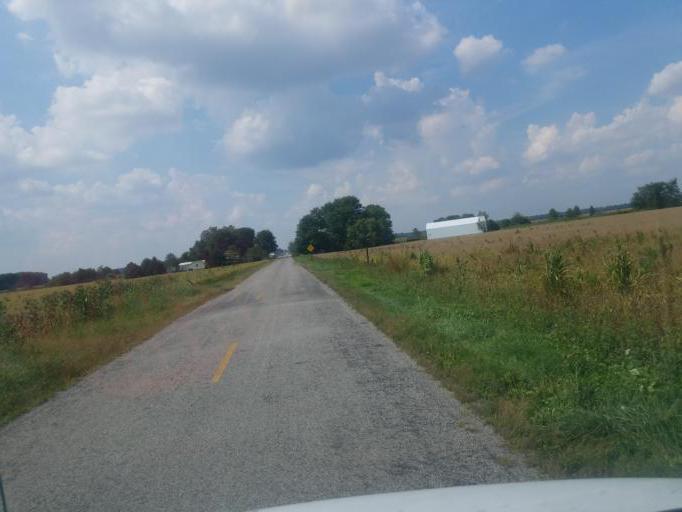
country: US
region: Ohio
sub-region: Hardin County
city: Ada
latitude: 40.6376
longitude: -83.8035
